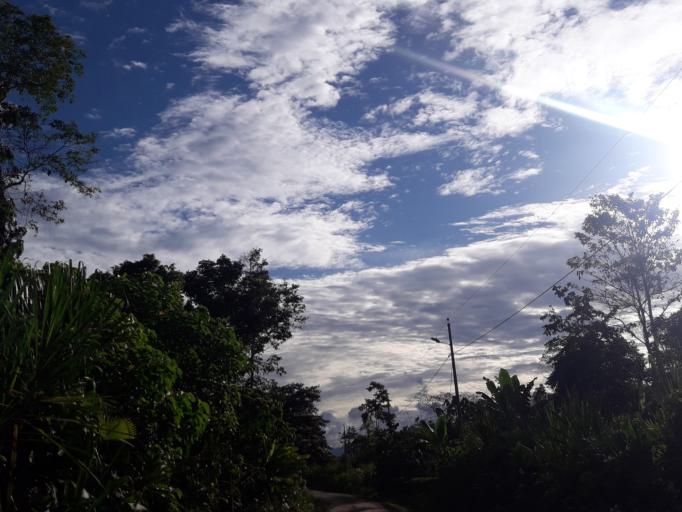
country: EC
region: Orellana
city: Boca Suno
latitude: -0.8834
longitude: -77.2941
